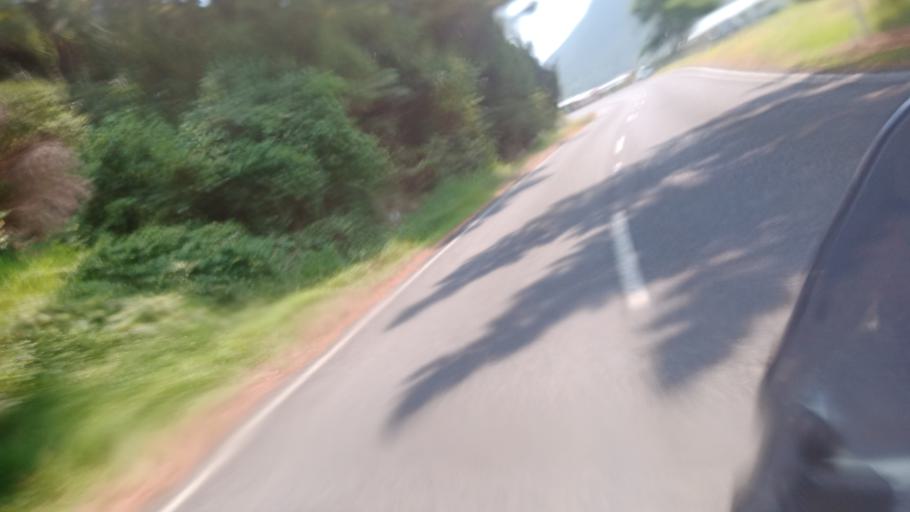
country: NZ
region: Bay of Plenty
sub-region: Opotiki District
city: Opotiki
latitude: -37.5727
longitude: 178.0139
